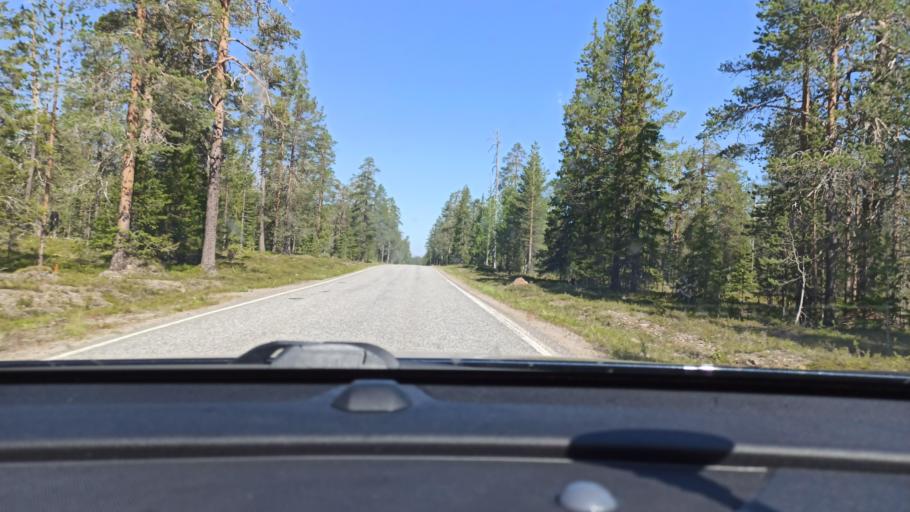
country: FI
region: Lapland
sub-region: Tunturi-Lappi
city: Kolari
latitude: 67.6605
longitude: 24.1656
